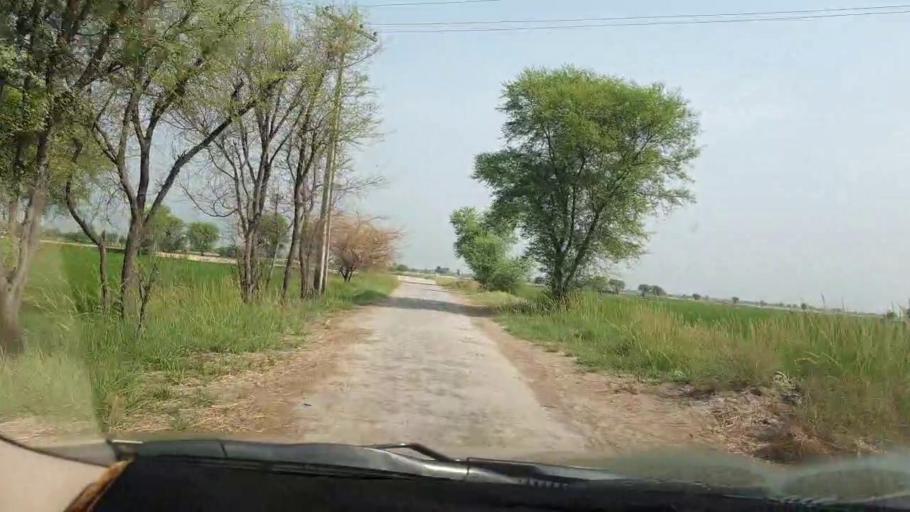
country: PK
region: Sindh
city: Goth Garelo
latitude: 27.4518
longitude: 68.0200
